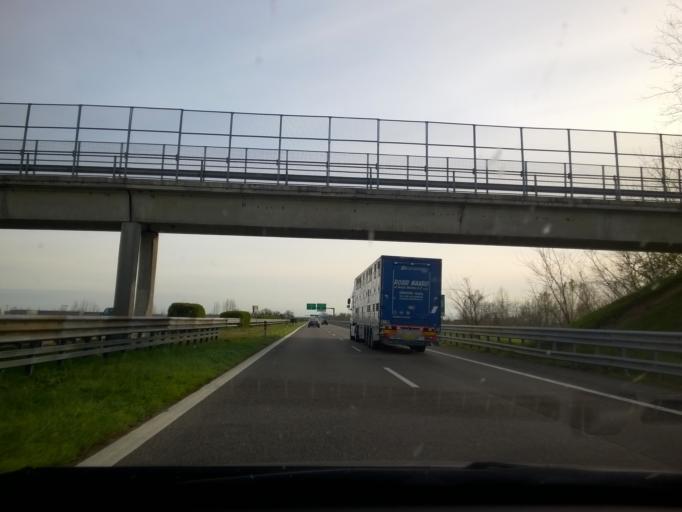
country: IT
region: Lombardy
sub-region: Provincia di Brescia
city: Alfianello
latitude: 45.2818
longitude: 10.1322
